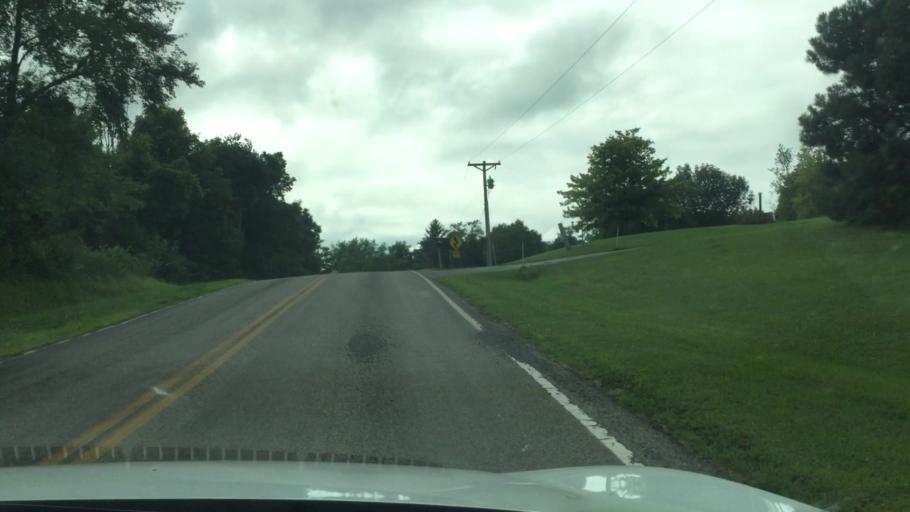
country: US
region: Ohio
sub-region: Champaign County
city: Mechanicsburg
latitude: 40.0604
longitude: -83.6349
